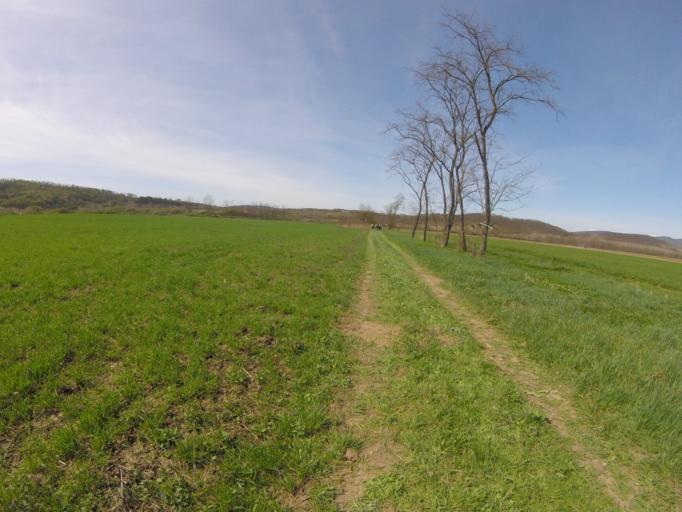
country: HU
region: Borsod-Abauj-Zemplen
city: Szendro
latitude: 48.4178
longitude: 20.7648
